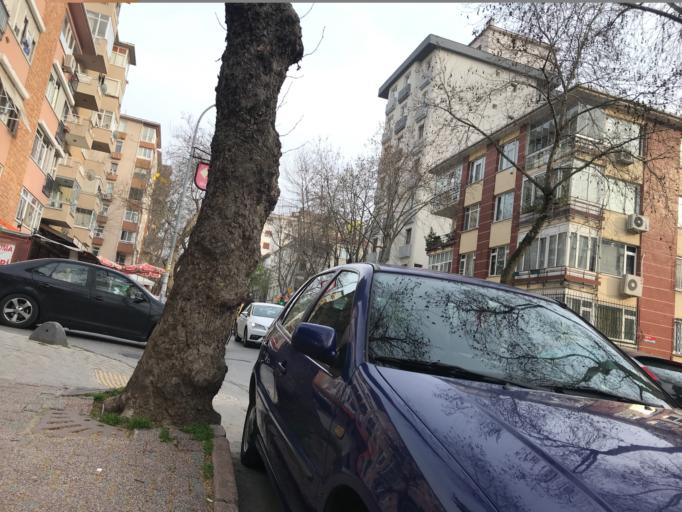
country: TR
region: Istanbul
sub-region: Atasehir
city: Atasehir
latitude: 40.9596
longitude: 29.0927
